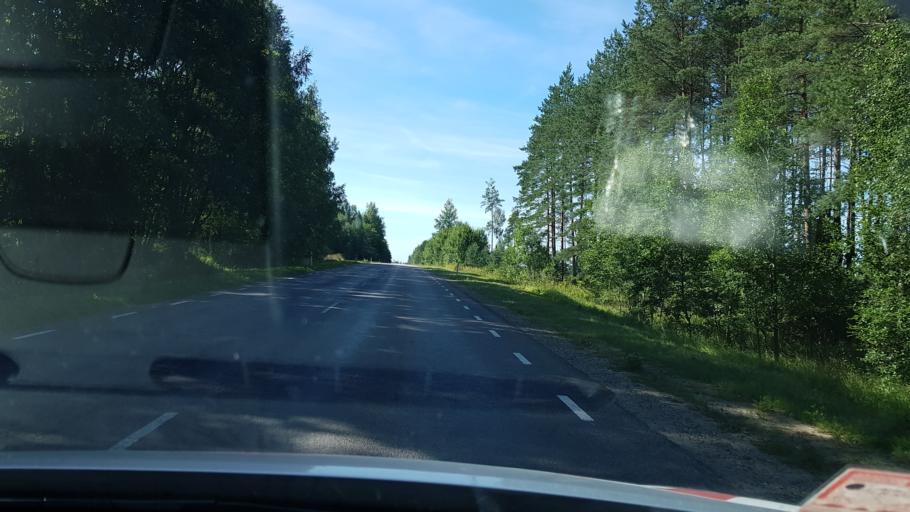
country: EE
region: Tartu
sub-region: Alatskivi vald
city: Kallaste
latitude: 58.5251
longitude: 27.0072
